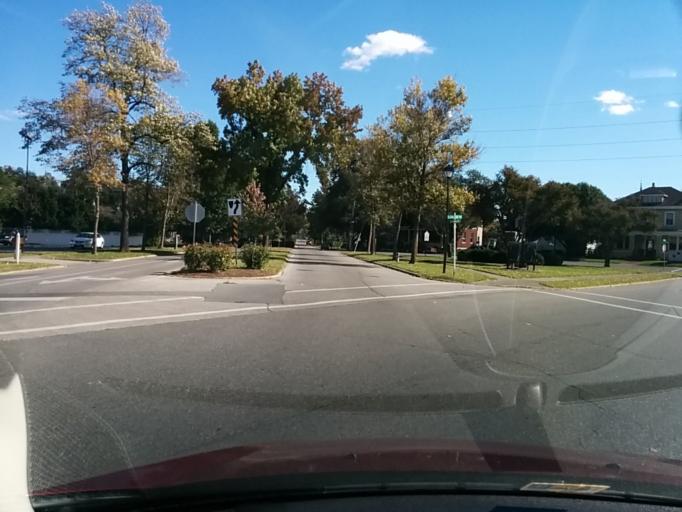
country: US
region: Virginia
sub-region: City of Salem
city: Salem
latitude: 37.2901
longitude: -80.0538
